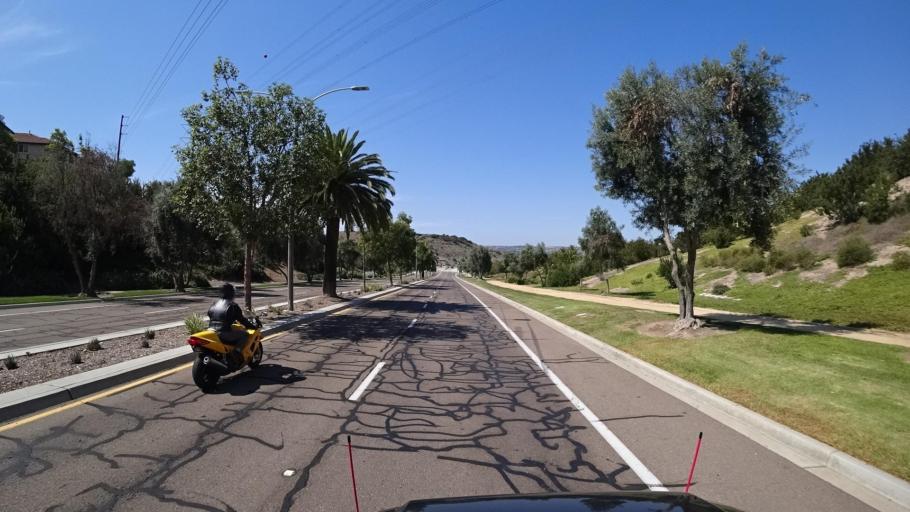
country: US
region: California
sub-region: San Diego County
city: La Presa
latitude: 32.6707
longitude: -116.9815
